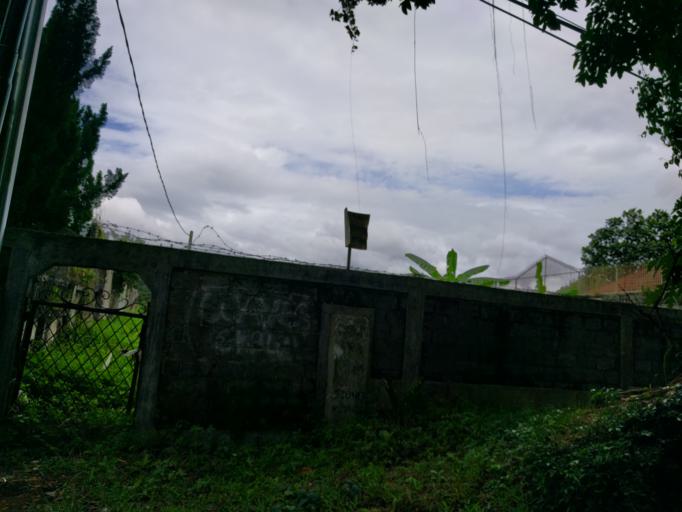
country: ID
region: West Java
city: Bogor
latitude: -6.5916
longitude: 106.8035
